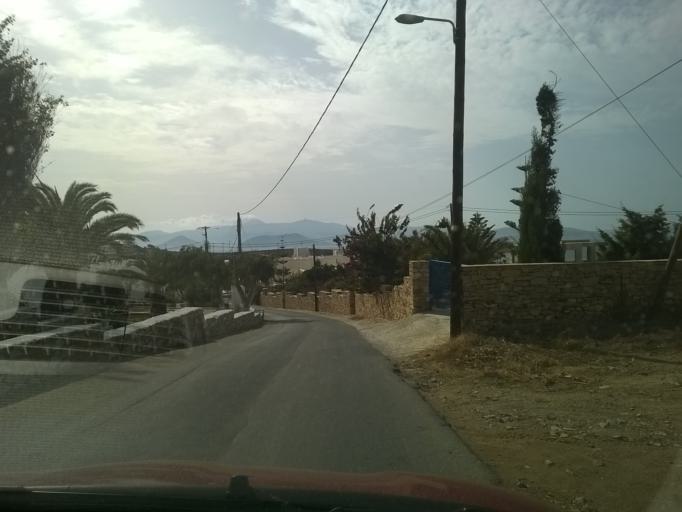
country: GR
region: South Aegean
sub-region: Nomos Kykladon
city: Naxos
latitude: 37.0817
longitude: 25.3446
